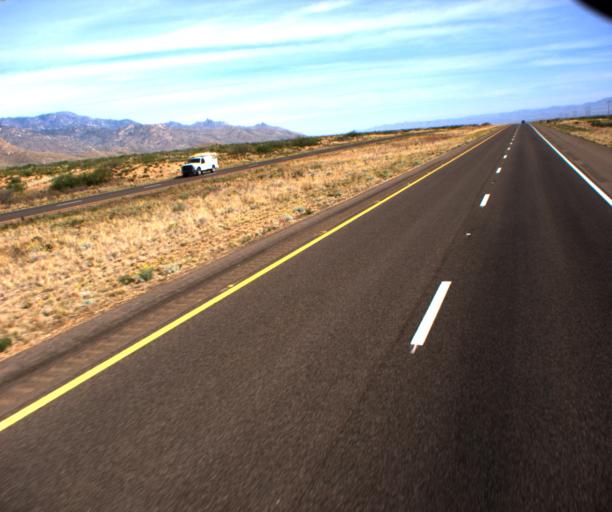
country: US
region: Arizona
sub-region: Graham County
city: Swift Trail Junction
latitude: 32.5584
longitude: -109.6787
